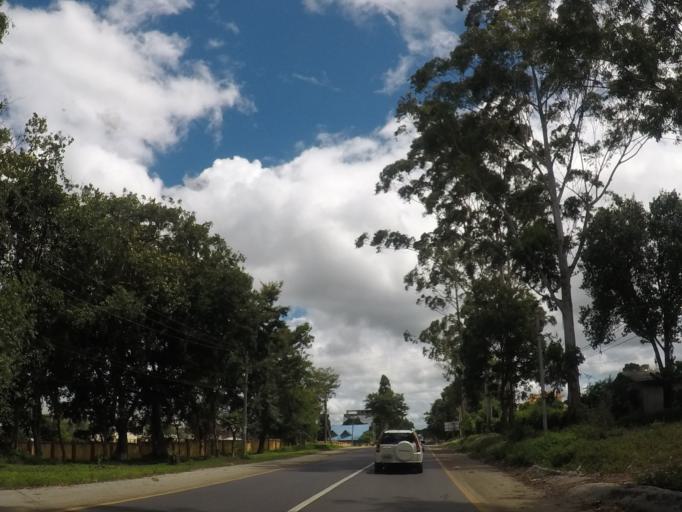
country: MM
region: Mandalay
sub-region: Pyin Oo Lwin District
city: Pyin Oo Lwin
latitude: 22.0544
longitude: 96.5098
